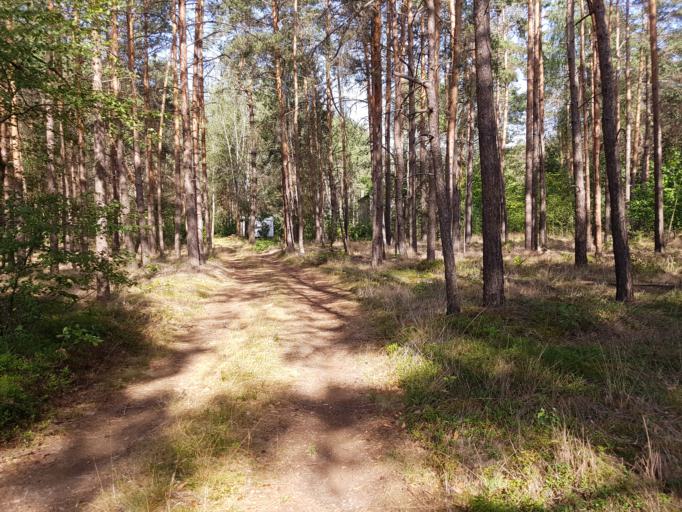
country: DE
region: Brandenburg
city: Finsterwalde
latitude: 51.6234
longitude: 13.6665
